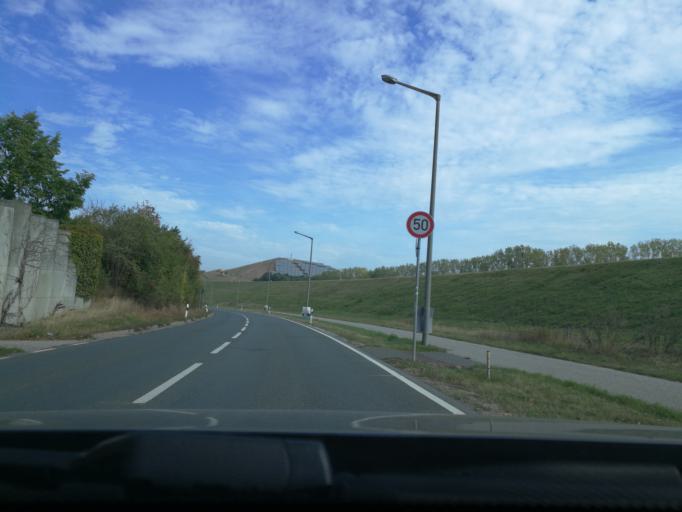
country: DE
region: Bavaria
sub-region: Regierungsbezirk Mittelfranken
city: Furth
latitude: 49.5047
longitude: 10.9559
